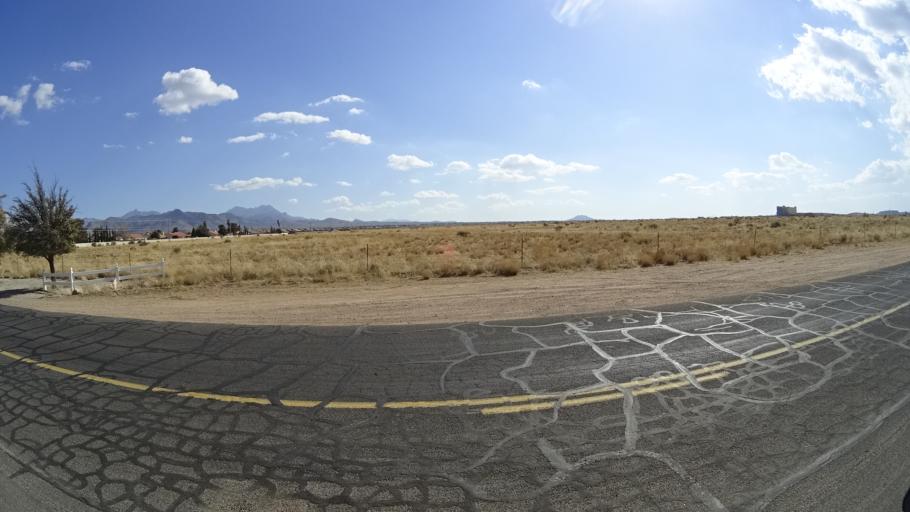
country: US
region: Arizona
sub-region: Mohave County
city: New Kingman-Butler
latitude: 35.2249
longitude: -113.9776
